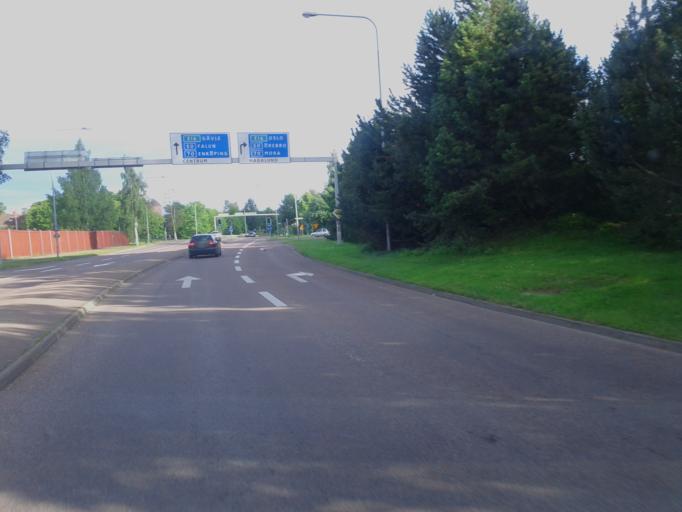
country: SE
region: Dalarna
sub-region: Borlange Kommun
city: Borlaenge
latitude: 60.4951
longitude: 15.4311
